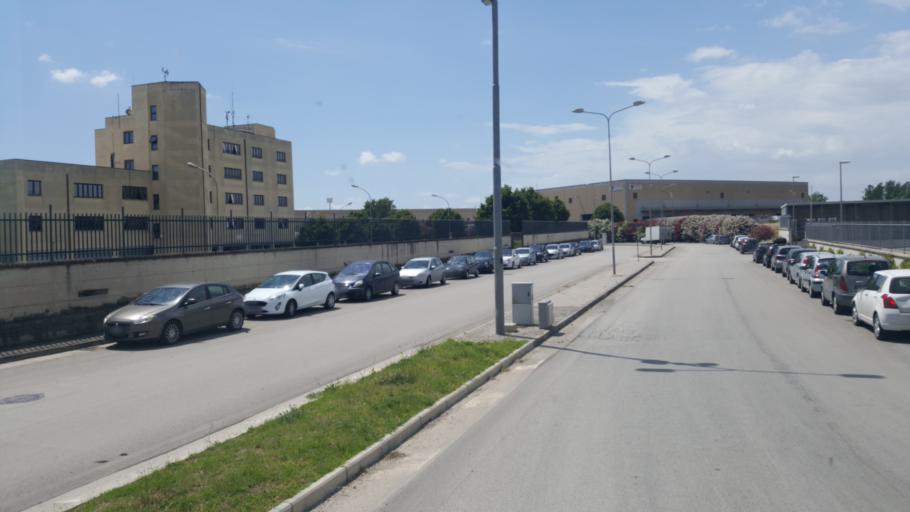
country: IT
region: Campania
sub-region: Provincia di Caserta
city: Maddaloni
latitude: 41.0095
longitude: 14.3672
